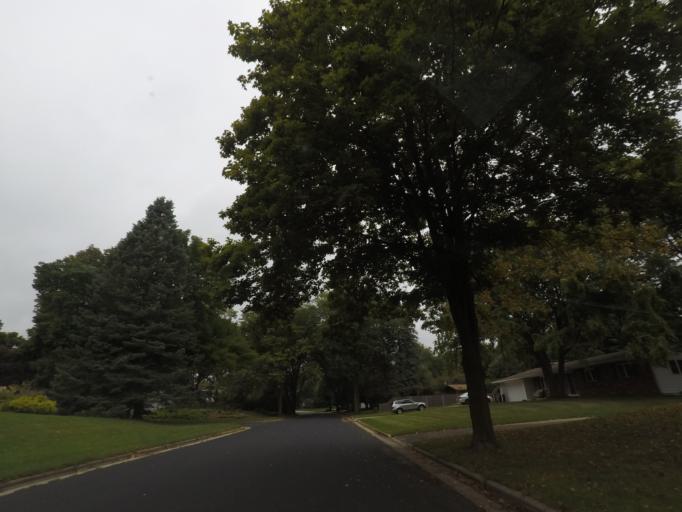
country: US
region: Wisconsin
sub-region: Dane County
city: Shorewood Hills
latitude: 43.0368
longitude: -89.4657
